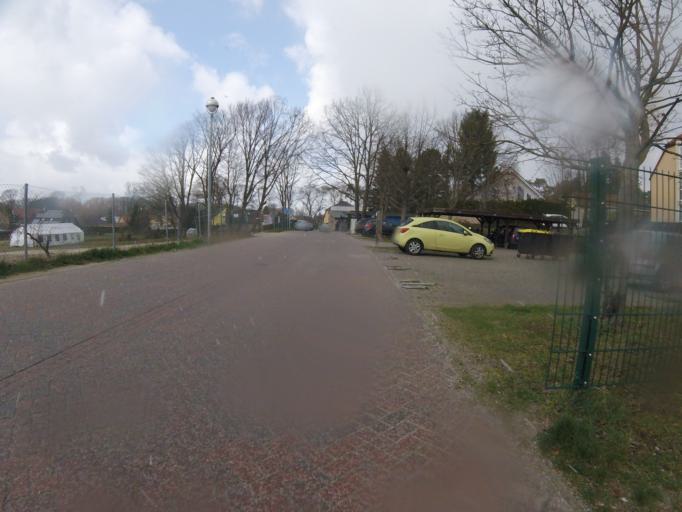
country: DE
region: Brandenburg
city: Mittenwalde
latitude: 52.2047
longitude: 13.5851
